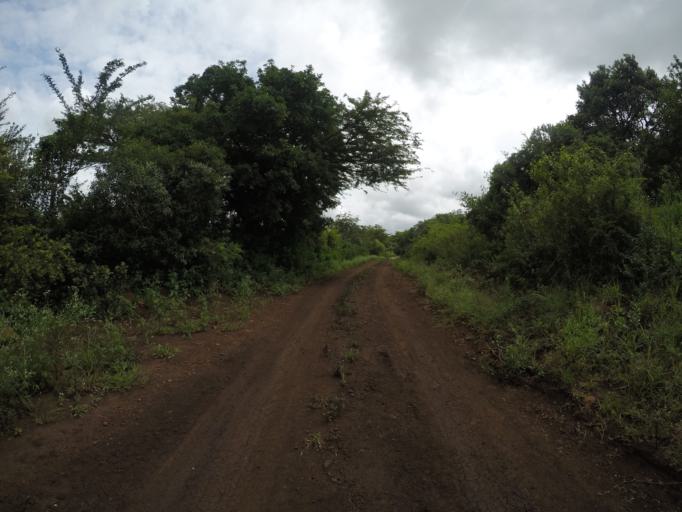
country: ZA
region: KwaZulu-Natal
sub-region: uThungulu District Municipality
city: Empangeni
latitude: -28.5913
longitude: 31.8729
